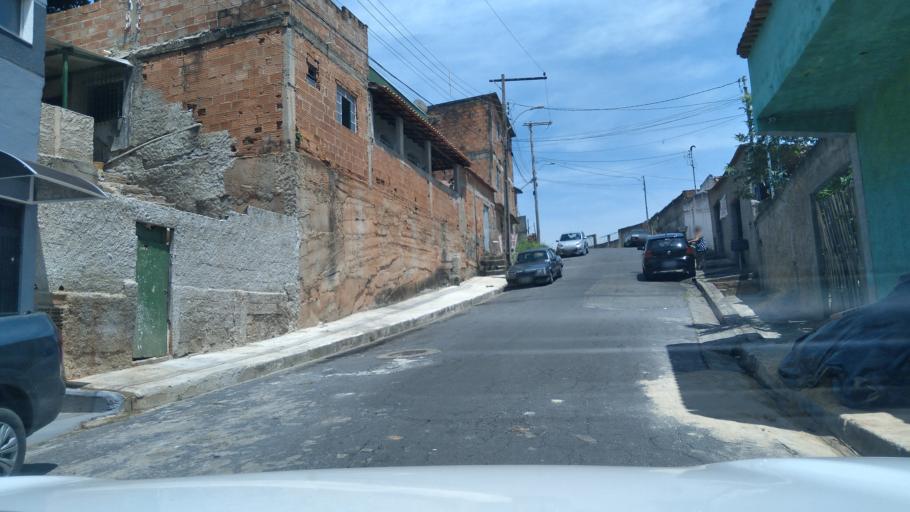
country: BR
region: Minas Gerais
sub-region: Contagem
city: Contagem
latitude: -19.9192
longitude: -44.0215
